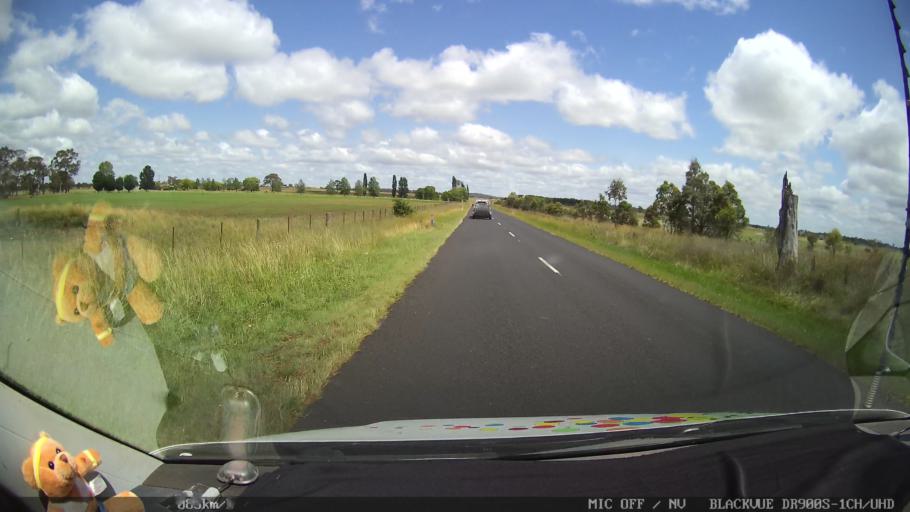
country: AU
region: New South Wales
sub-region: Glen Innes Severn
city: Glen Innes
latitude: -29.6843
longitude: 151.7020
